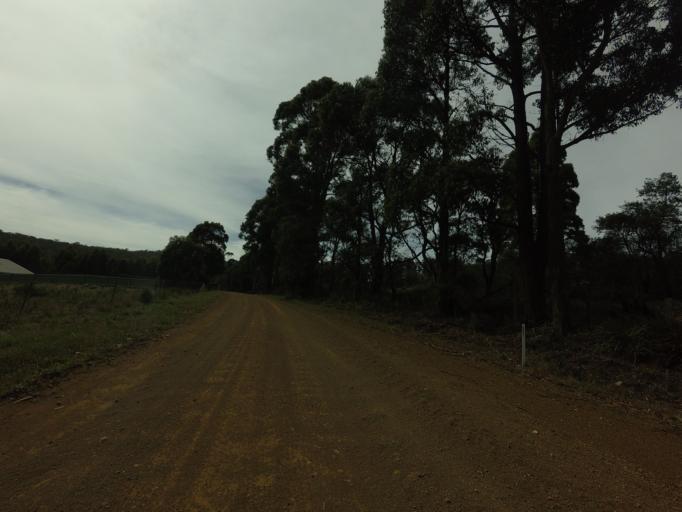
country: AU
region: Tasmania
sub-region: Sorell
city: Sorell
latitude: -42.4784
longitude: 147.6062
